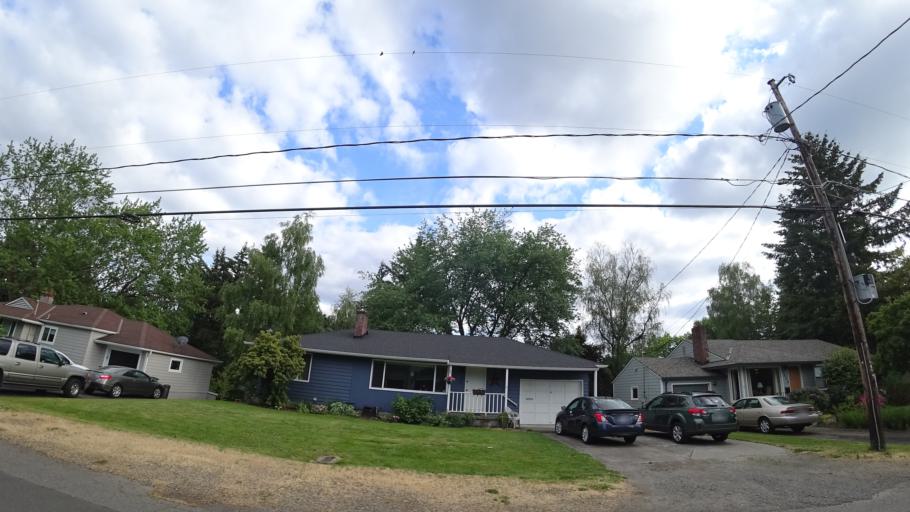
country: US
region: Oregon
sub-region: Washington County
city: Raleigh Hills
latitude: 45.4790
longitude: -122.7310
